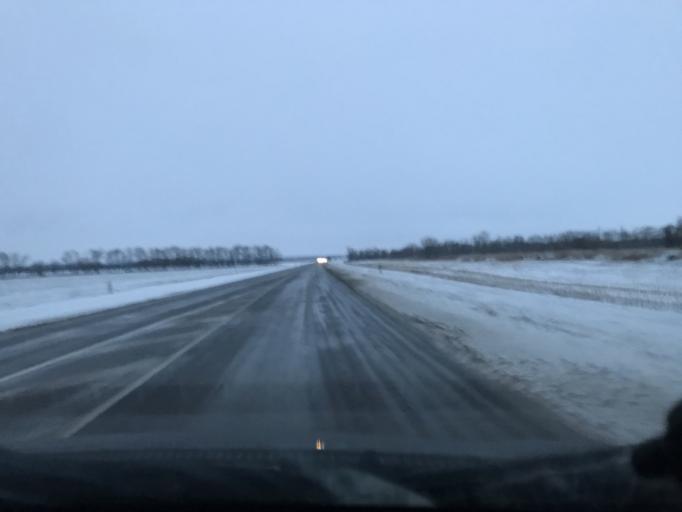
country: RU
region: Rostov
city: Letnik
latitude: 45.9737
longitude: 41.2527
